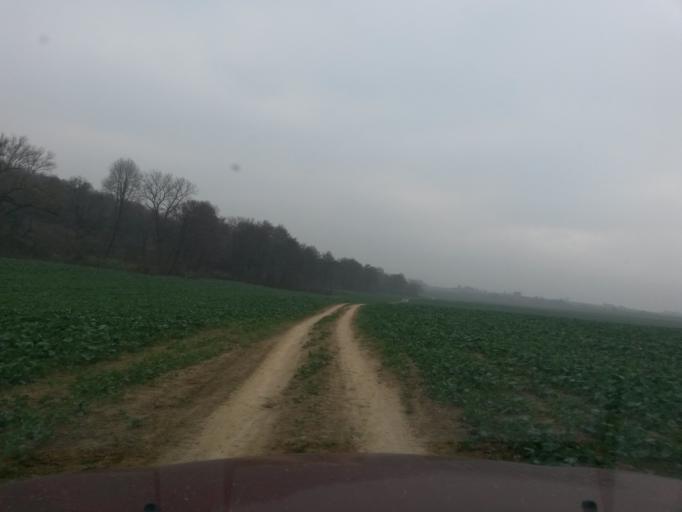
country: SK
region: Presovsky
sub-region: Okres Presov
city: Presov
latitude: 48.8867
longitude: 21.2872
